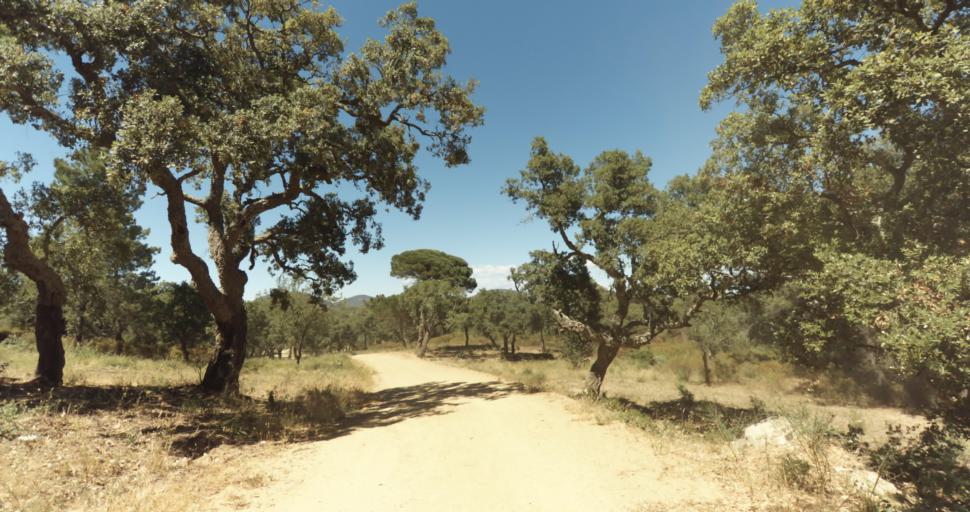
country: FR
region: Provence-Alpes-Cote d'Azur
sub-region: Departement du Var
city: Gassin
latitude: 43.2513
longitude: 6.5645
